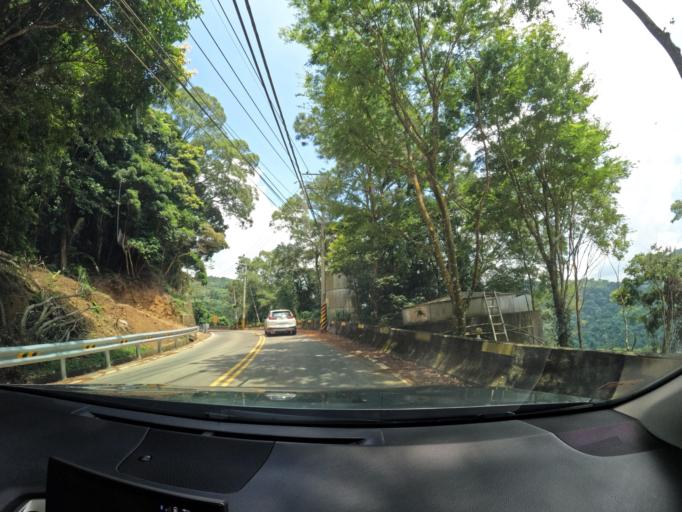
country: TW
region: Taiwan
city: Fengyuan
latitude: 24.3870
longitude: 120.8156
